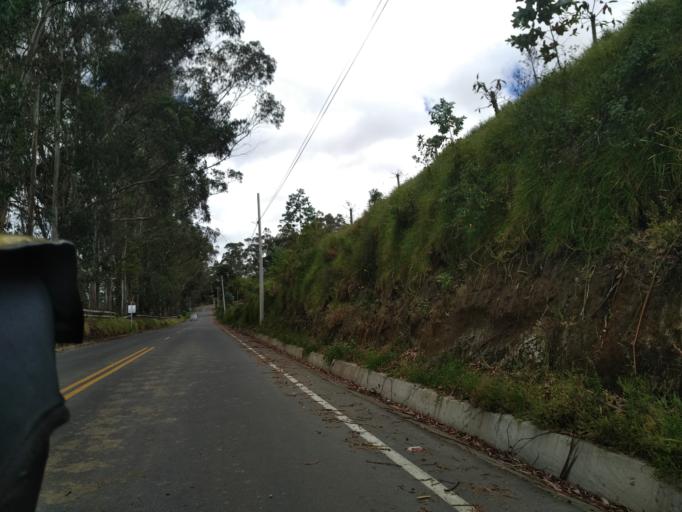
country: EC
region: Cotopaxi
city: Saquisili
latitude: -0.7181
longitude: -78.8868
